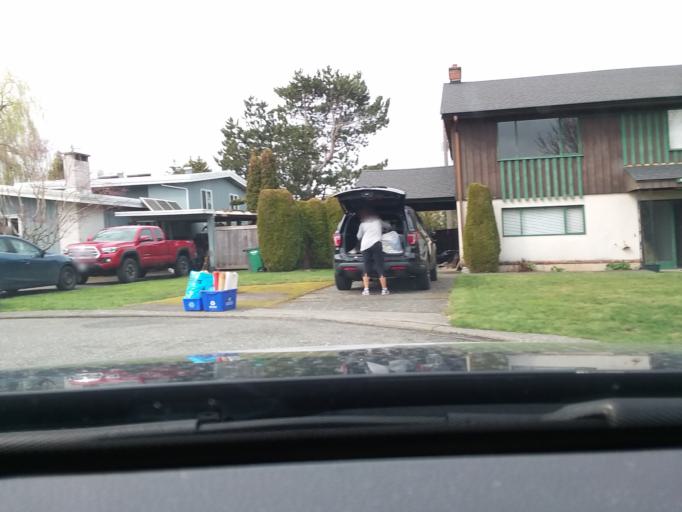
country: CA
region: British Columbia
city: Oak Bay
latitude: 48.4736
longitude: -123.3281
